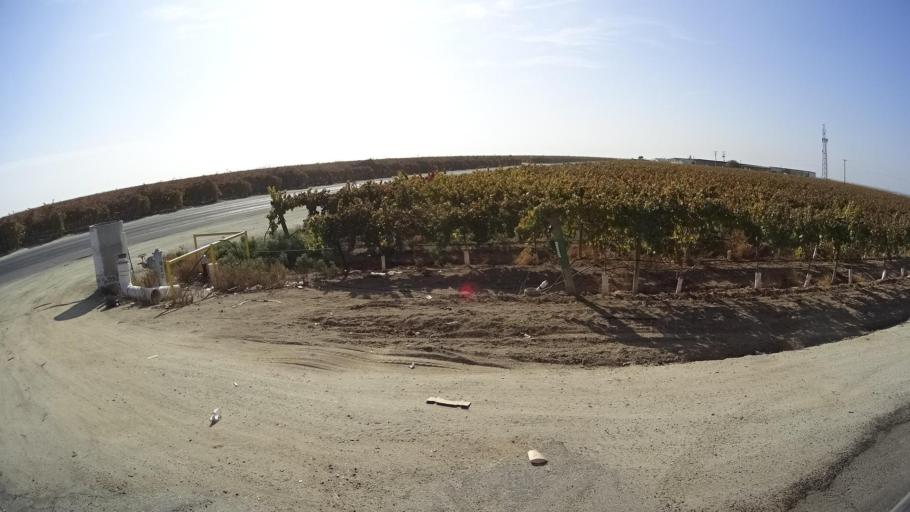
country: US
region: California
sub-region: Kern County
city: McFarland
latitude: 35.6891
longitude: -119.1778
